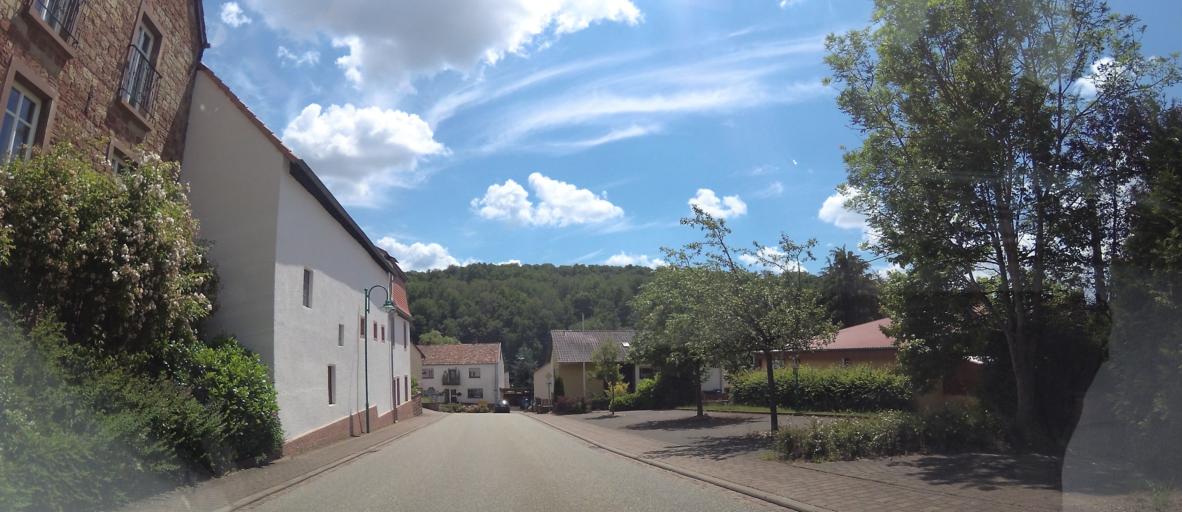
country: DE
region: Rheinland-Pfalz
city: Walshausen
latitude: 49.2108
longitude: 7.4760
